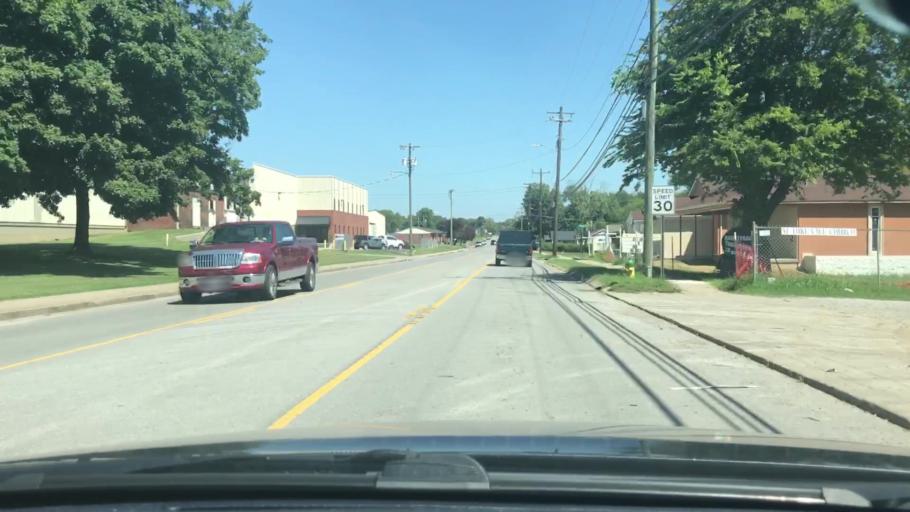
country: US
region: Tennessee
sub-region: Sumner County
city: Gallatin
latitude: 36.3930
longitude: -86.4527
